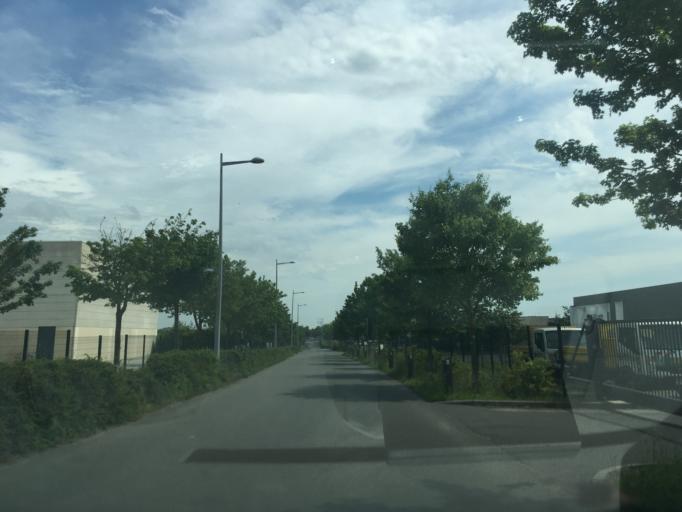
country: FR
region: Poitou-Charentes
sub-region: Departement de la Charente
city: Saint-Brice
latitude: 45.6769
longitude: -0.3083
